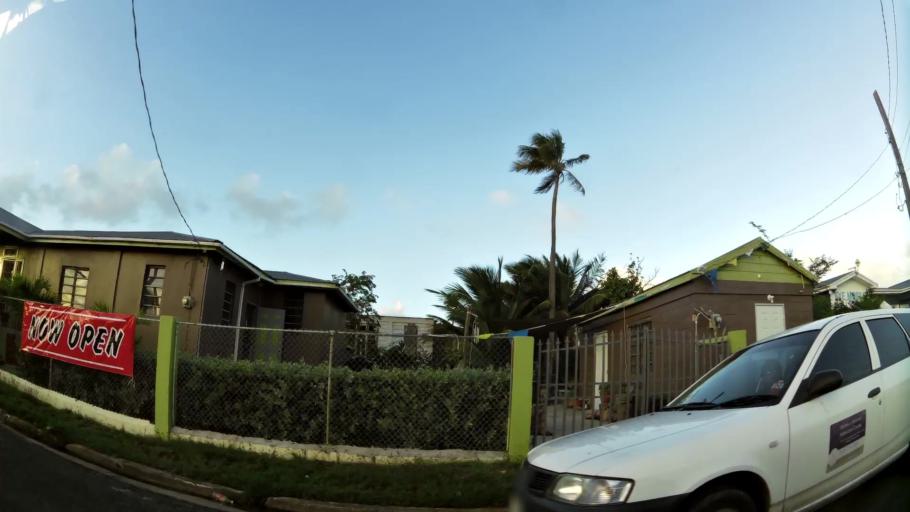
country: AG
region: Saint John
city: Saint John's
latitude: 17.1273
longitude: -61.8438
